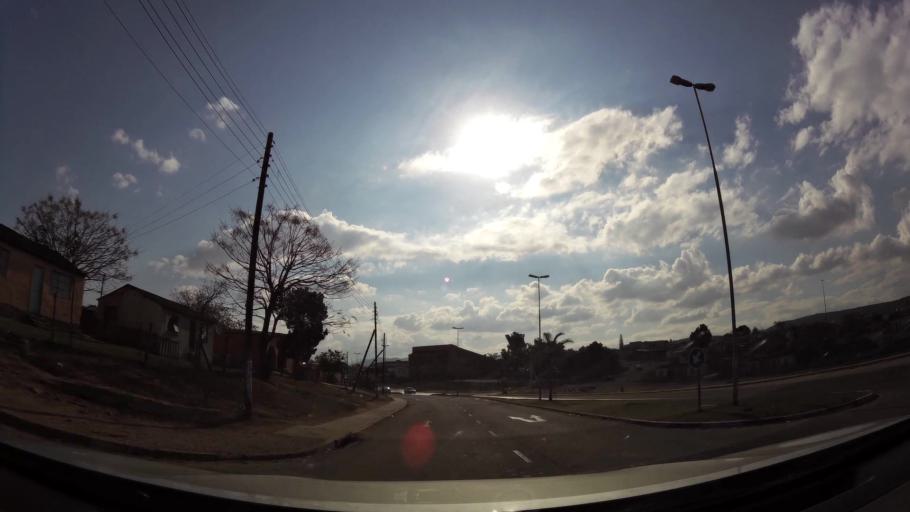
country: ZA
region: Eastern Cape
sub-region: Nelson Mandela Bay Metropolitan Municipality
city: Uitenhage
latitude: -33.7446
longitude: 25.3799
